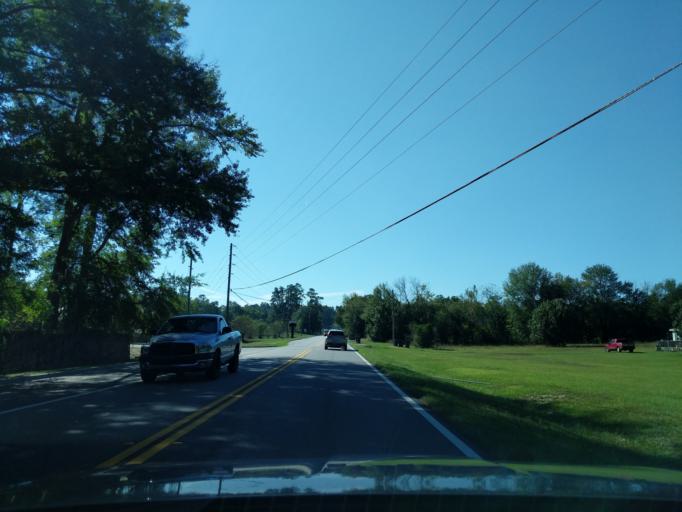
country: US
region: Georgia
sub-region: Richmond County
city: Hephzibah
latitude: 33.3401
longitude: -82.0064
